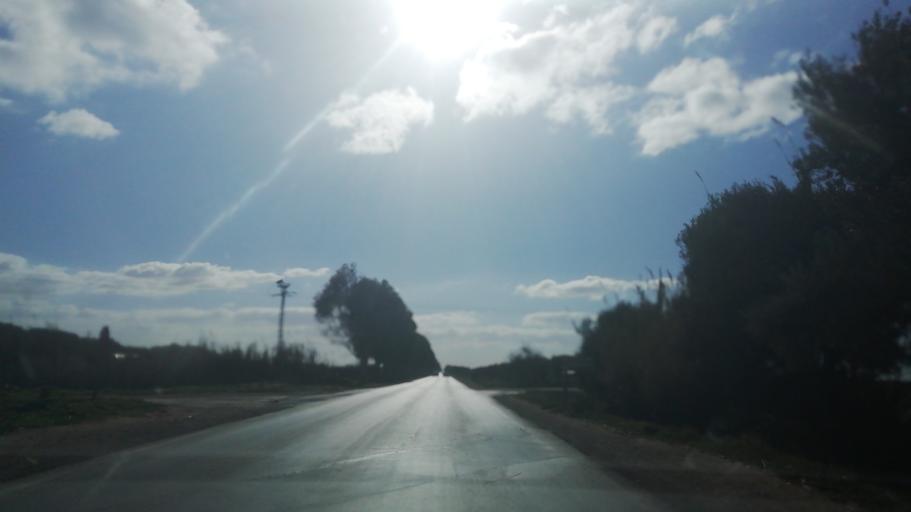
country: DZ
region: Mostaganem
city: Mostaganem
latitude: 35.9872
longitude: 0.2893
